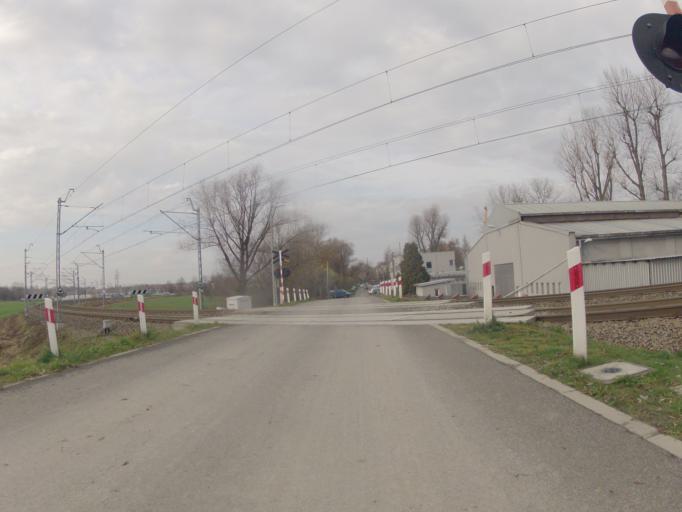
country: PL
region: Lesser Poland Voivodeship
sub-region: Powiat krakowski
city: Rzaska
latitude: 50.0802
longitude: 19.8538
